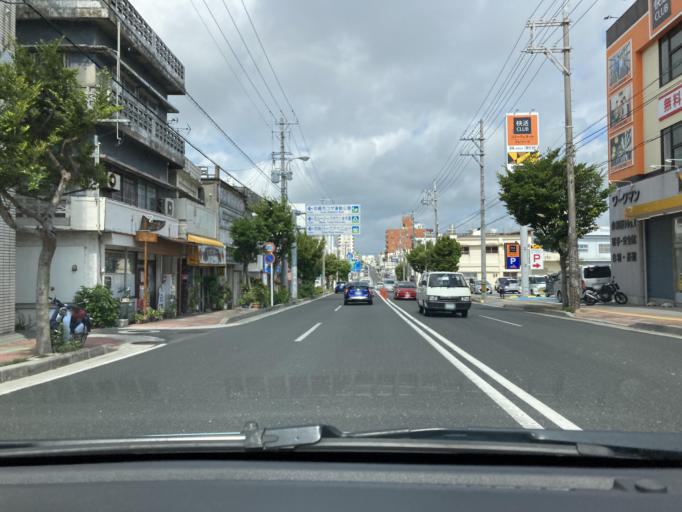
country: JP
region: Okinawa
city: Okinawa
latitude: 26.3373
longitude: 127.8166
